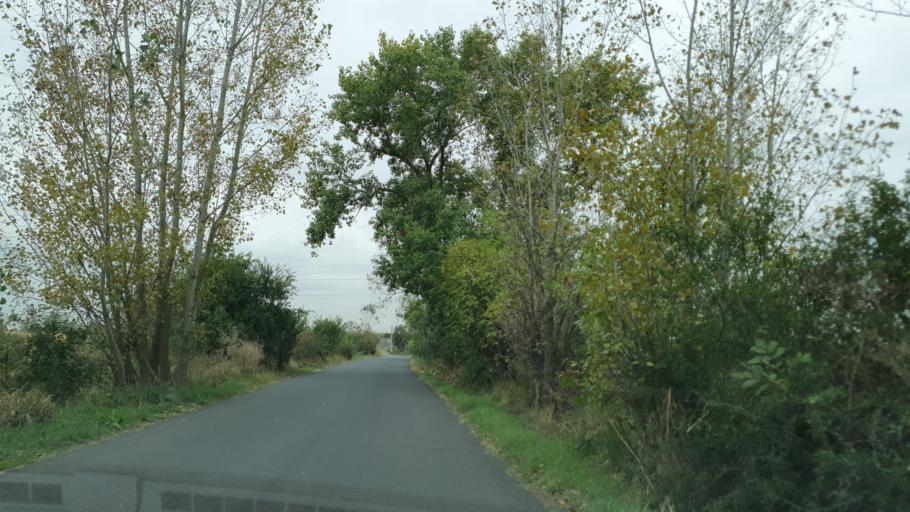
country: HU
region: Pest
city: Dunaharaszti
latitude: 47.3809
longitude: 19.0852
